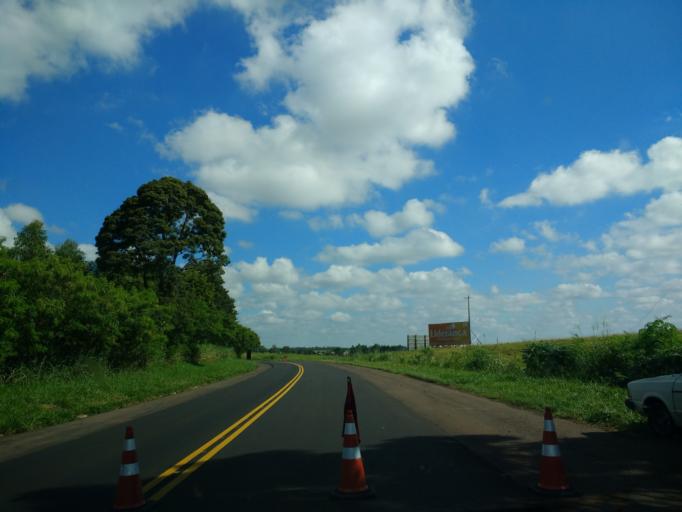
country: BR
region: Parana
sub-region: Umuarama
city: Umuarama
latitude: -23.8676
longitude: -53.3926
